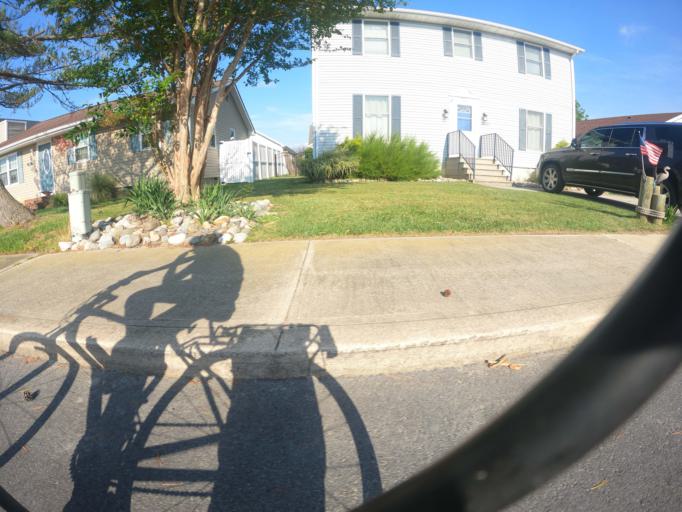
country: US
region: Delaware
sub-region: Sussex County
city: Bethany Beach
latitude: 38.4443
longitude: -75.0612
